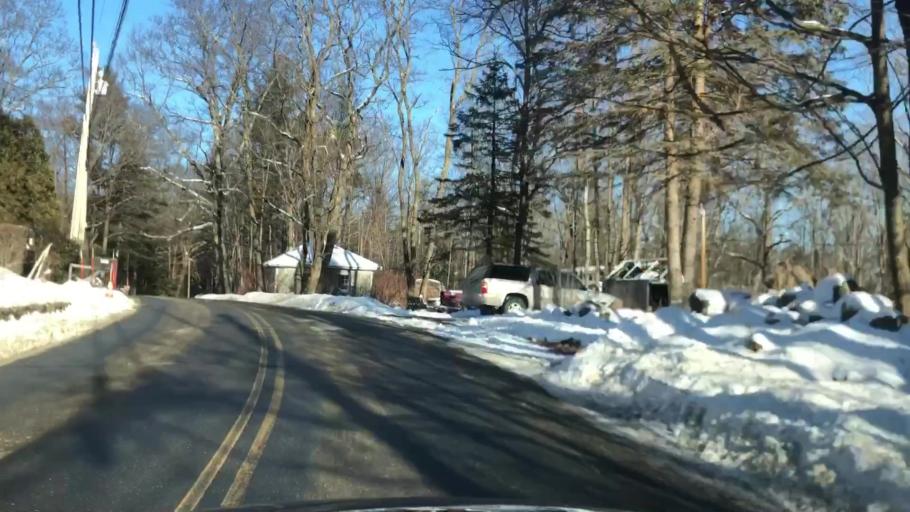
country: US
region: New Hampshire
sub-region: Hillsborough County
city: Wilton
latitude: 42.8125
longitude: -71.7019
